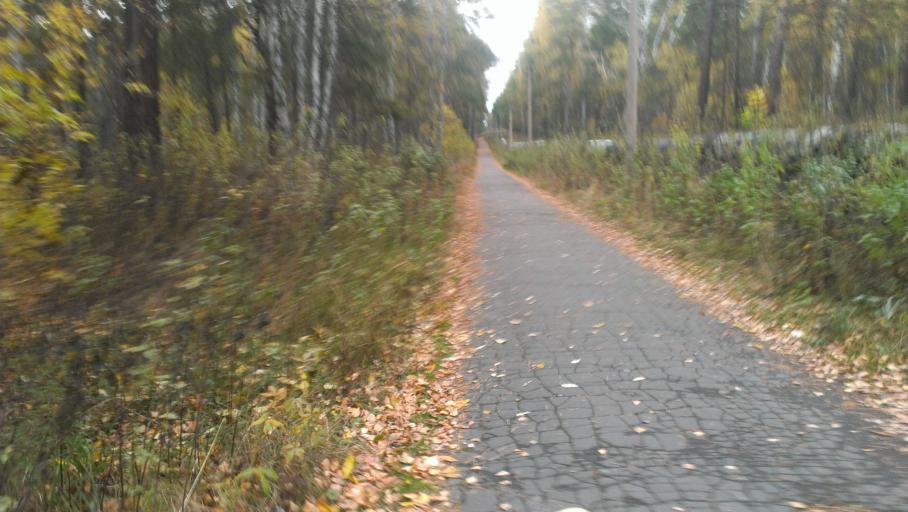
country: RU
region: Altai Krai
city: Yuzhnyy
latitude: 53.2628
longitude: 83.6866
